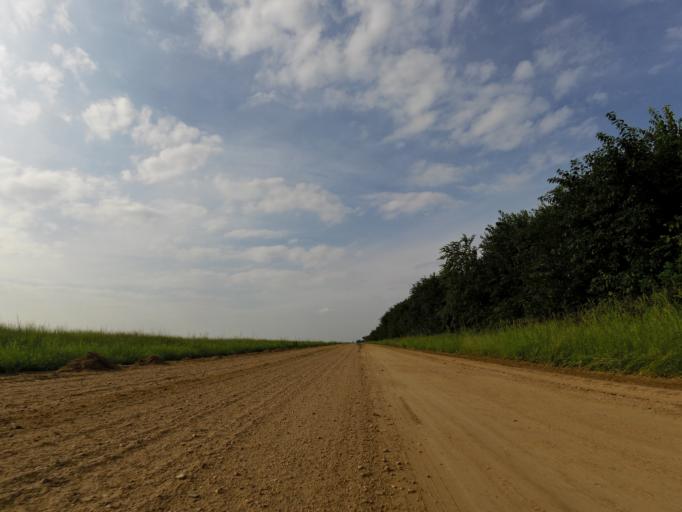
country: US
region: Kansas
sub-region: Reno County
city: South Hutchinson
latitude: 37.9587
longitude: -98.0689
